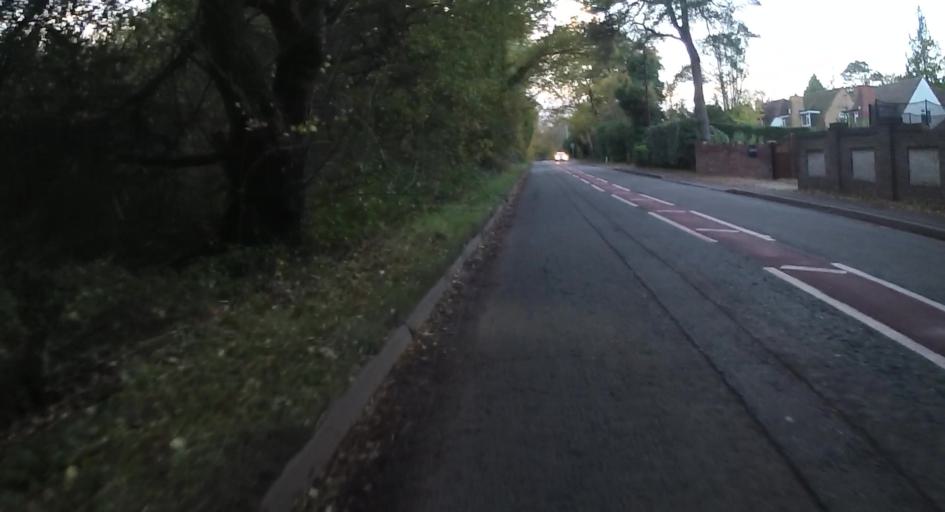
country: GB
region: England
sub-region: Wokingham
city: Finchampstead
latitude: 51.3756
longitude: -0.8715
